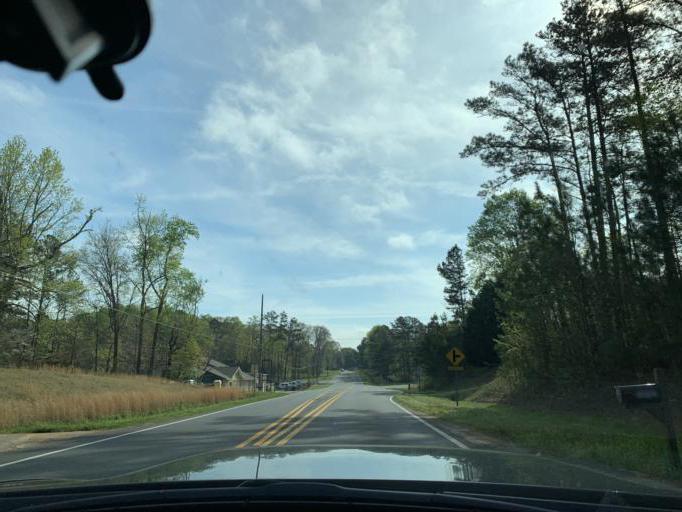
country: US
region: Georgia
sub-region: Forsyth County
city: Cumming
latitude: 34.2612
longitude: -84.1235
